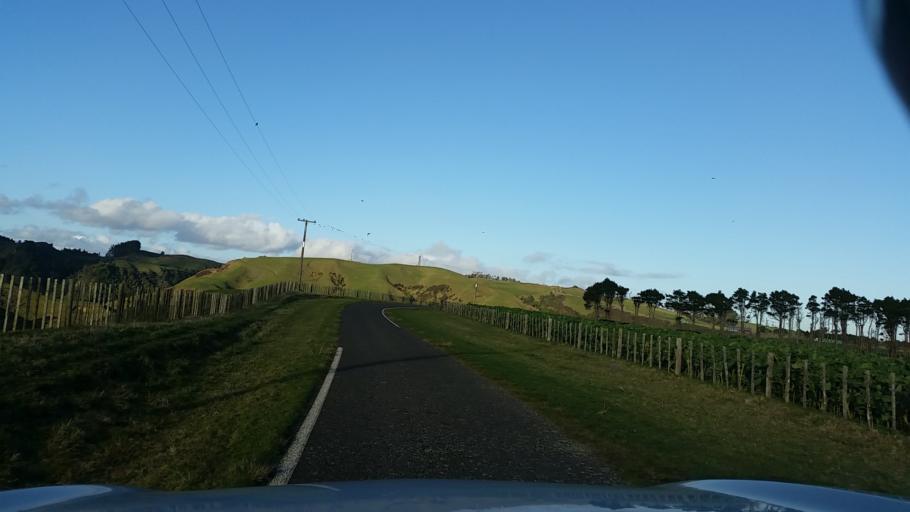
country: NZ
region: Taranaki
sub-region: South Taranaki District
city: Patea
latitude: -39.6263
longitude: 174.5062
